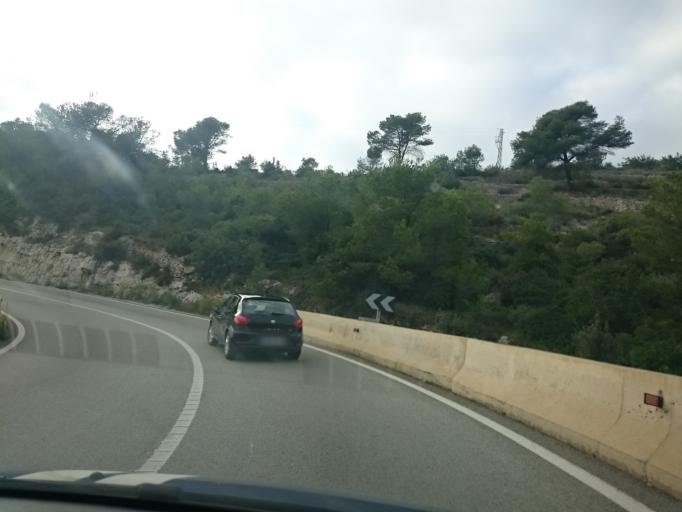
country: ES
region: Catalonia
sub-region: Provincia de Barcelona
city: Sitges
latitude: 41.2371
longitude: 1.8362
